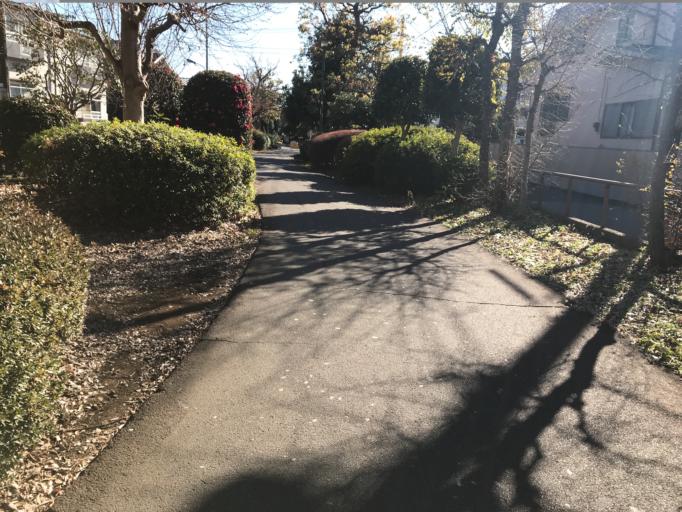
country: JP
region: Tokyo
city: Hino
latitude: 35.7119
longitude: 139.4241
